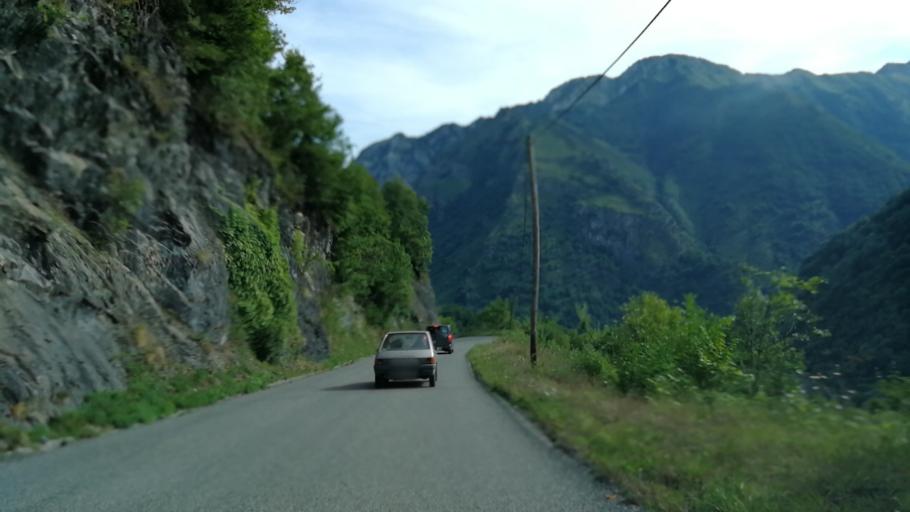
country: FR
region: Aquitaine
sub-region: Departement des Pyrenees-Atlantiques
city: Arette
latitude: 42.9362
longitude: -0.6250
